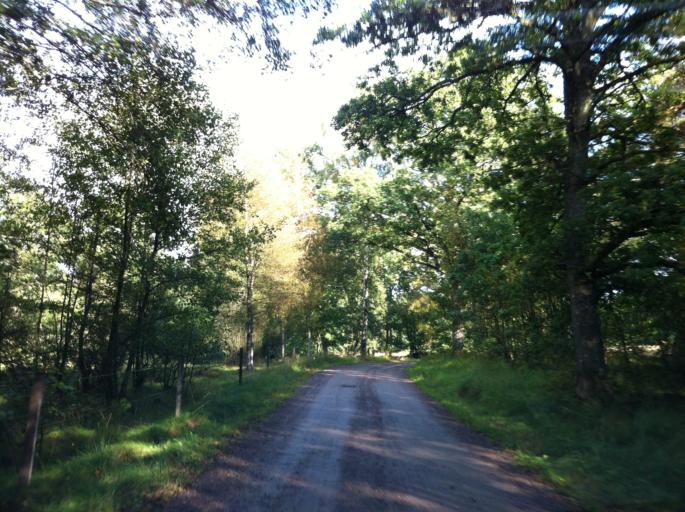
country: SE
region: Skane
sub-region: Hassleholms Kommun
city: Sosdala
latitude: 56.1258
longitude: 13.5933
